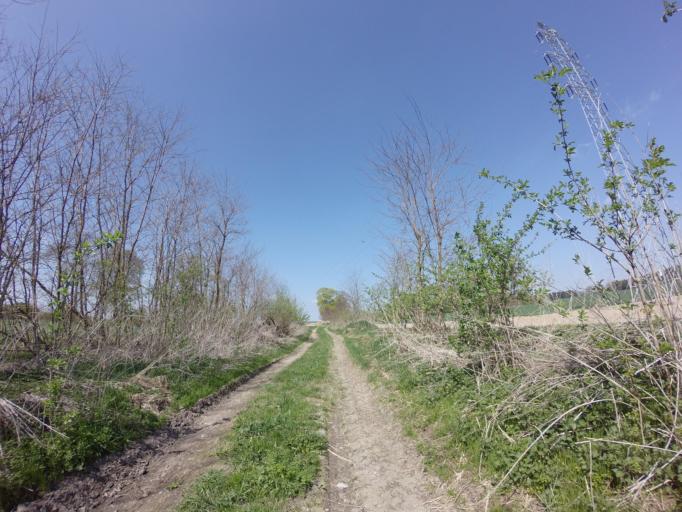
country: PL
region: West Pomeranian Voivodeship
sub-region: Powiat stargardzki
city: Suchan
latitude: 53.2125
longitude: 15.3547
